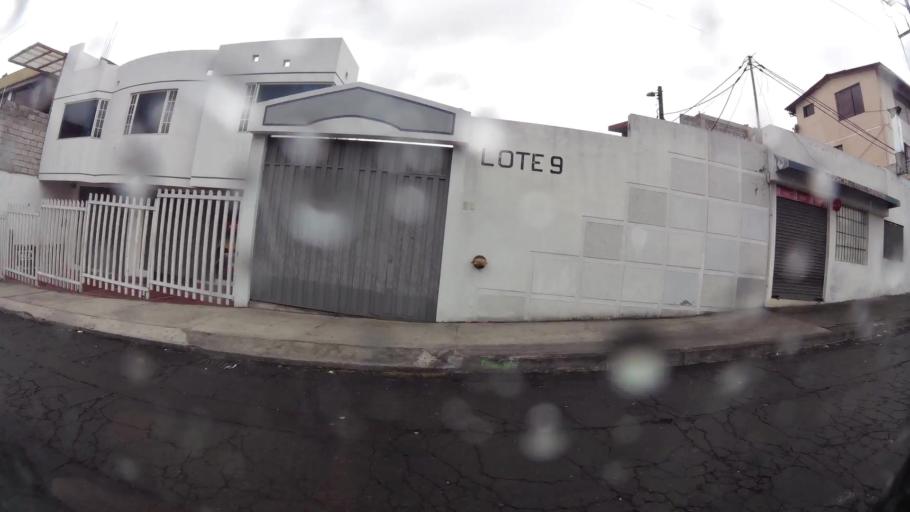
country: EC
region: Pichincha
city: Quito
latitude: -0.1224
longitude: -78.4982
